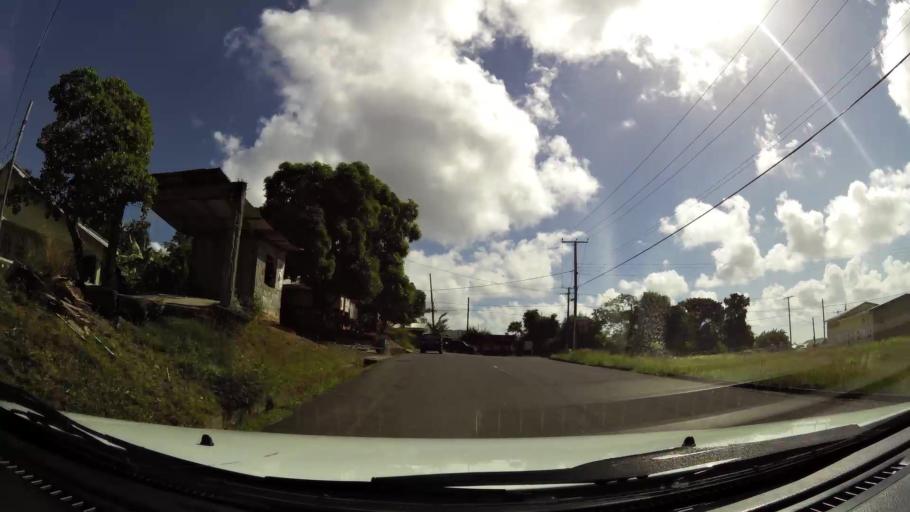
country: LC
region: Choiseul Quarter
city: Choiseul
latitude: 13.7752
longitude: -61.0322
